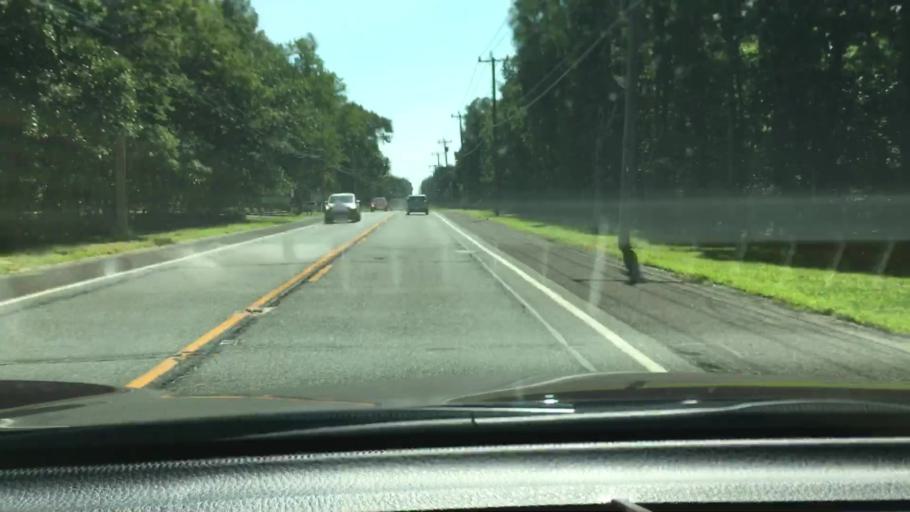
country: US
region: New Jersey
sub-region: Cumberland County
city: Millville
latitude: 39.3852
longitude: -74.9851
